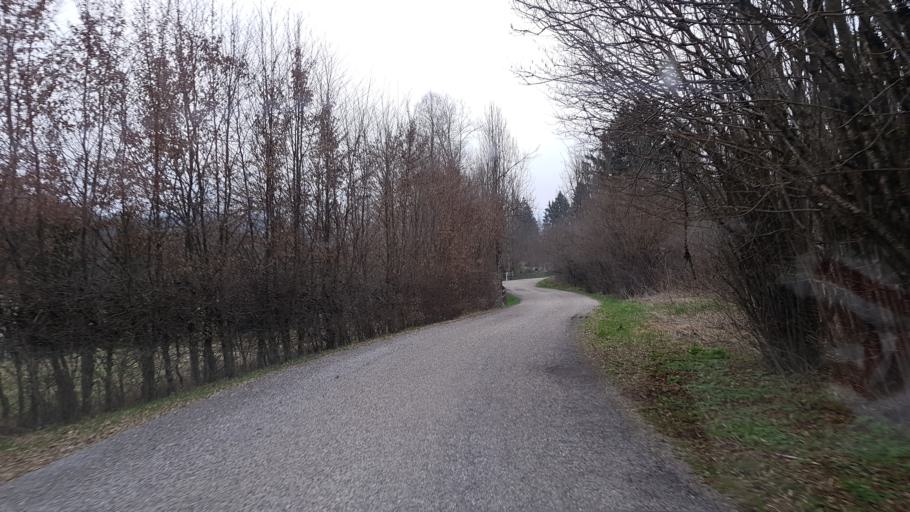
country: IT
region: Friuli Venezia Giulia
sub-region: Provincia di Udine
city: Faedis
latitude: 46.2001
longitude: 13.4014
